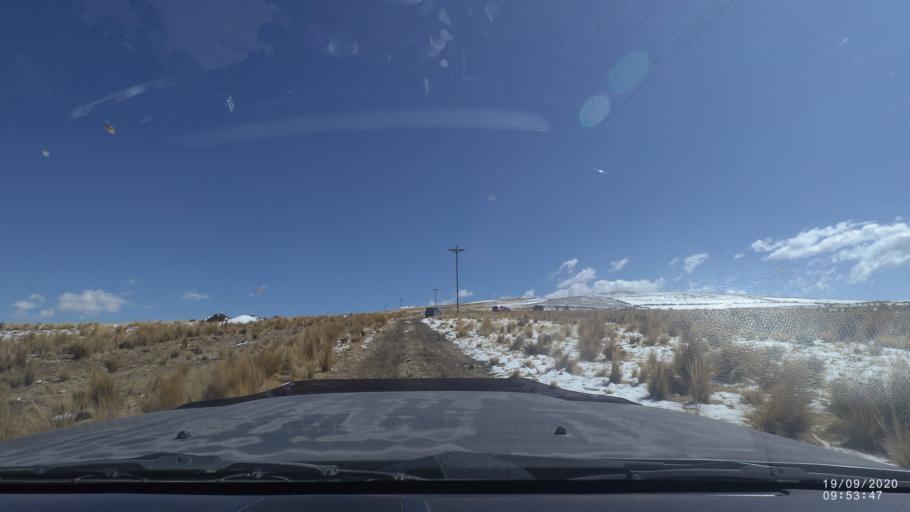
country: BO
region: Cochabamba
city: Cochabamba
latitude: -17.3160
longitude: -66.0821
